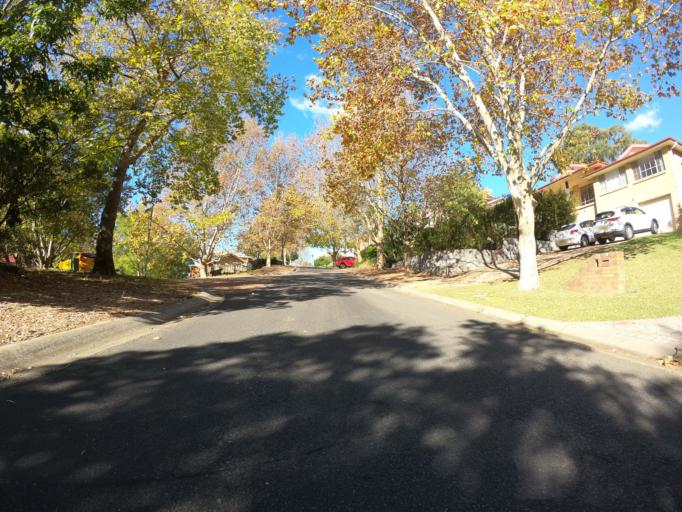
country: AU
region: New South Wales
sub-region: Wollongong
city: Mount Keira
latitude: -34.4155
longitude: 150.8477
